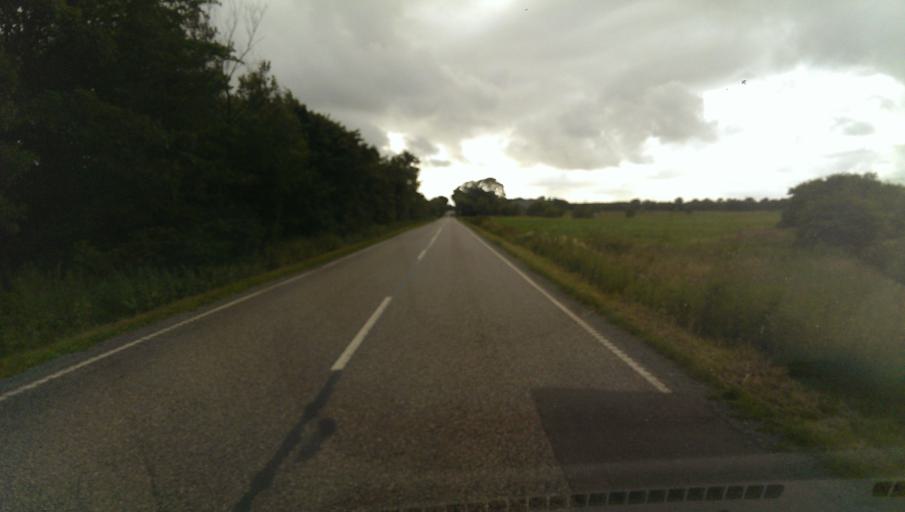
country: DK
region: South Denmark
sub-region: Esbjerg Kommune
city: Tjaereborg
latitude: 55.5188
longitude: 8.5231
